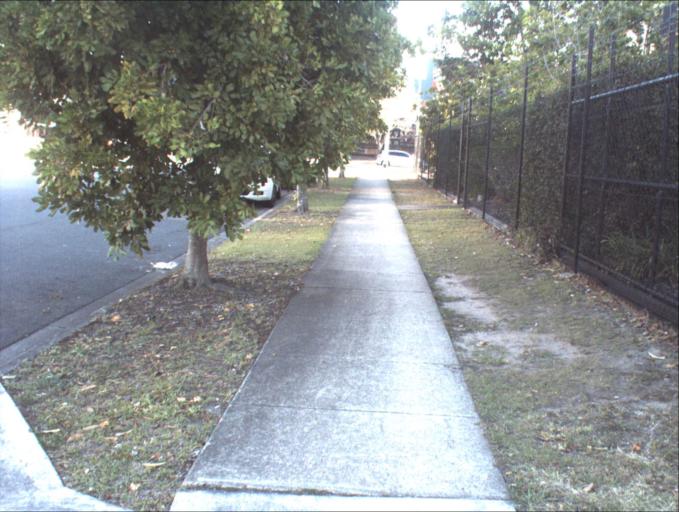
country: AU
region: Queensland
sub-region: Logan
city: Springwood
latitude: -27.6178
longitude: 153.1128
